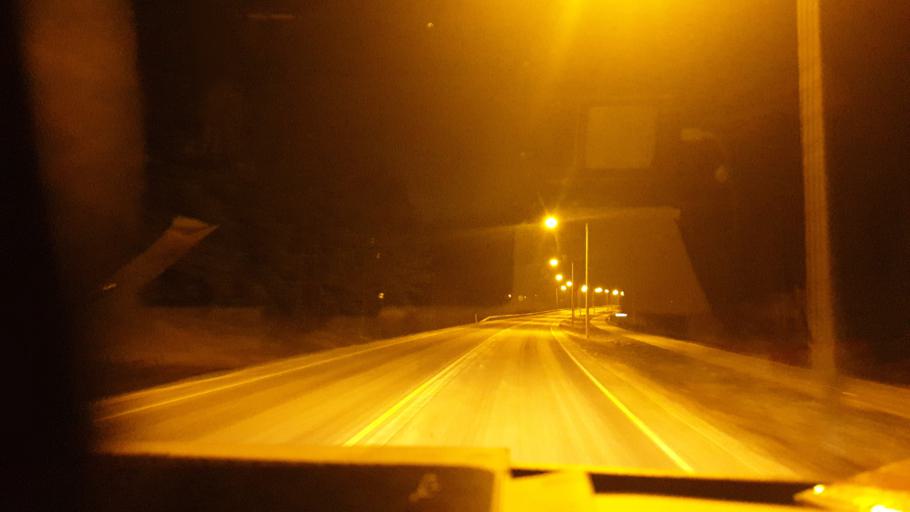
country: FI
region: Southern Ostrobothnia
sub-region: Kuusiokunnat
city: Alavus
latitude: 62.5970
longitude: 23.6555
